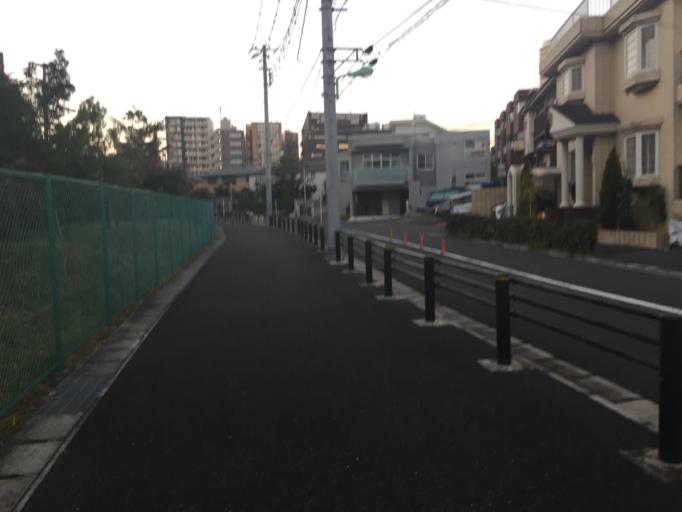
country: JP
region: Tokyo
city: Tokyo
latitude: 35.6294
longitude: 139.6597
